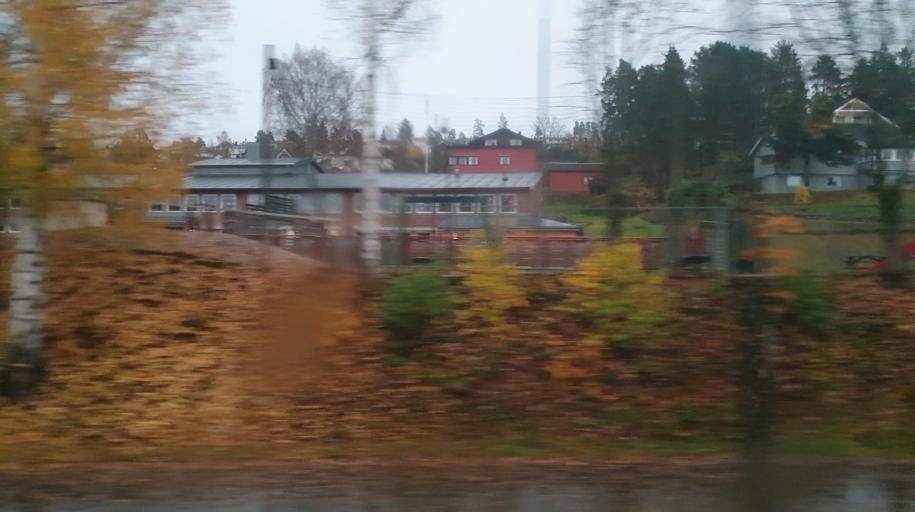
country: NO
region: Buskerud
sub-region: Modum
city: Vikersund
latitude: 59.8915
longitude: 9.9261
